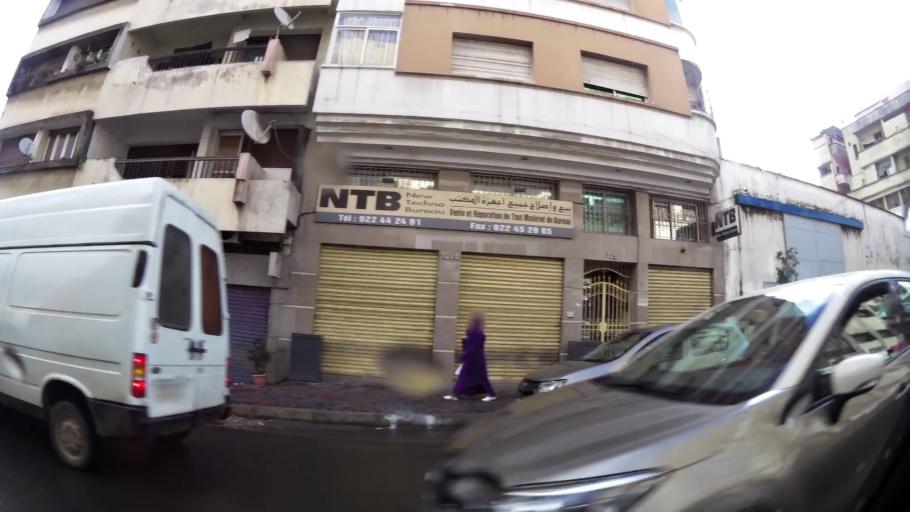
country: MA
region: Grand Casablanca
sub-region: Casablanca
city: Casablanca
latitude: 33.5843
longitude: -7.5998
